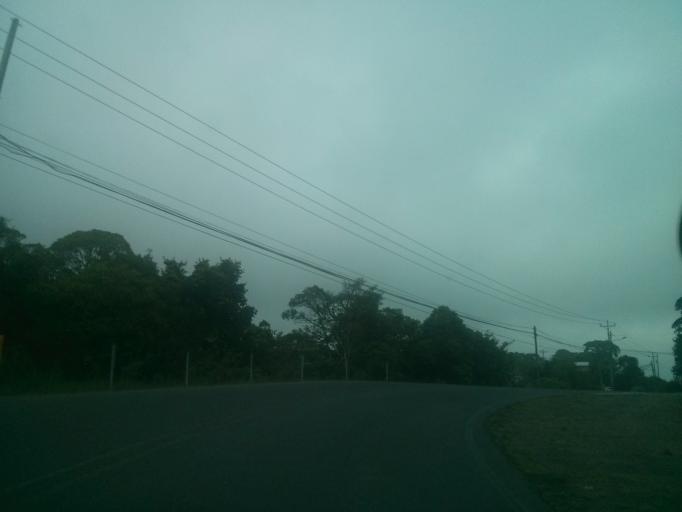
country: CR
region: Cartago
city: Cot
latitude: 9.8818
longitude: -83.8157
